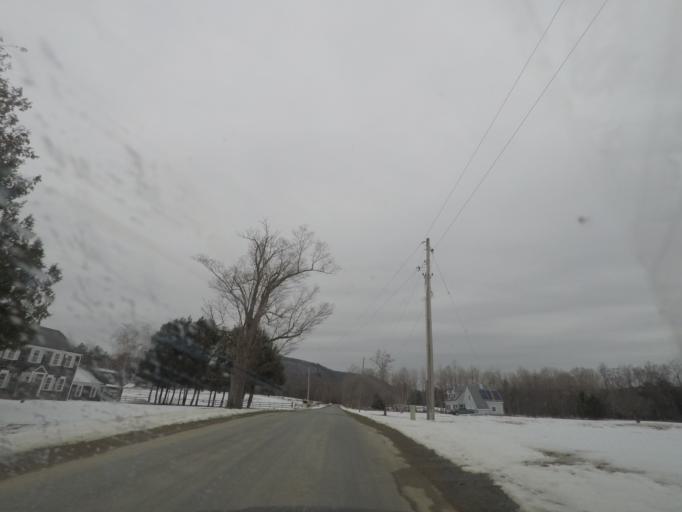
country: US
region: New York
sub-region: Rensselaer County
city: Averill Park
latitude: 42.5426
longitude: -73.4102
